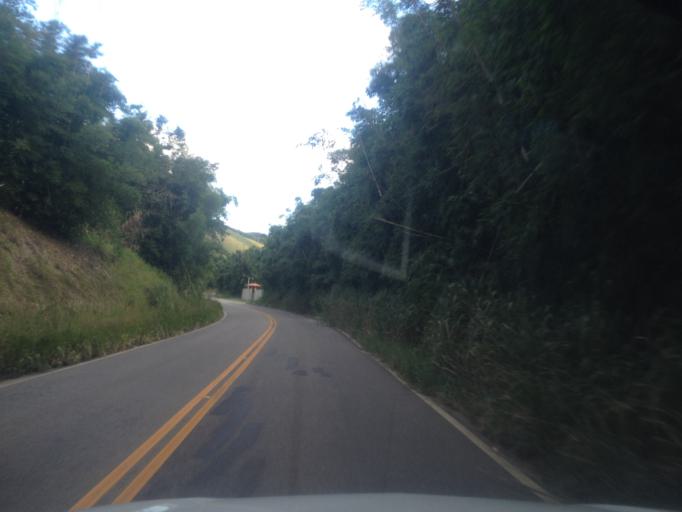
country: BR
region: Rio de Janeiro
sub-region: Quatis
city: Quatis
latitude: -22.3622
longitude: -44.2558
